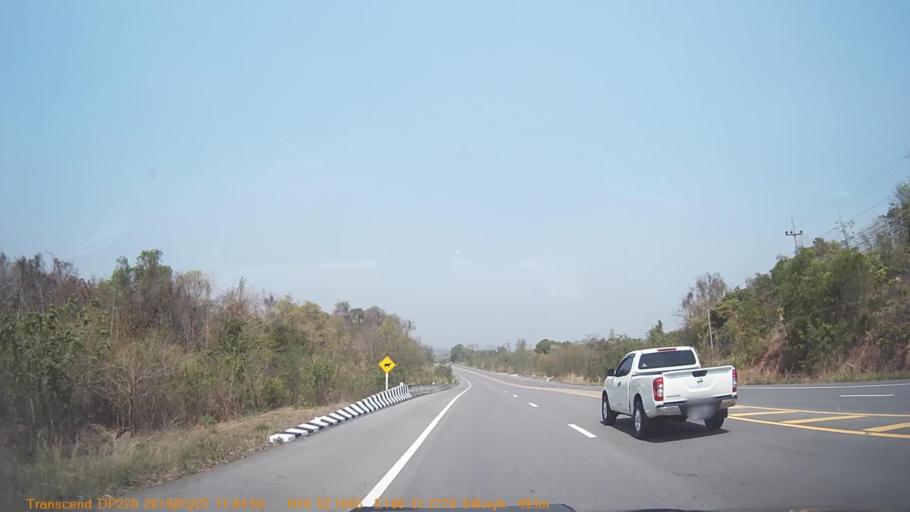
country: TH
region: Phitsanulok
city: Nakhon Thai
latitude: 16.8695
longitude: 100.8543
